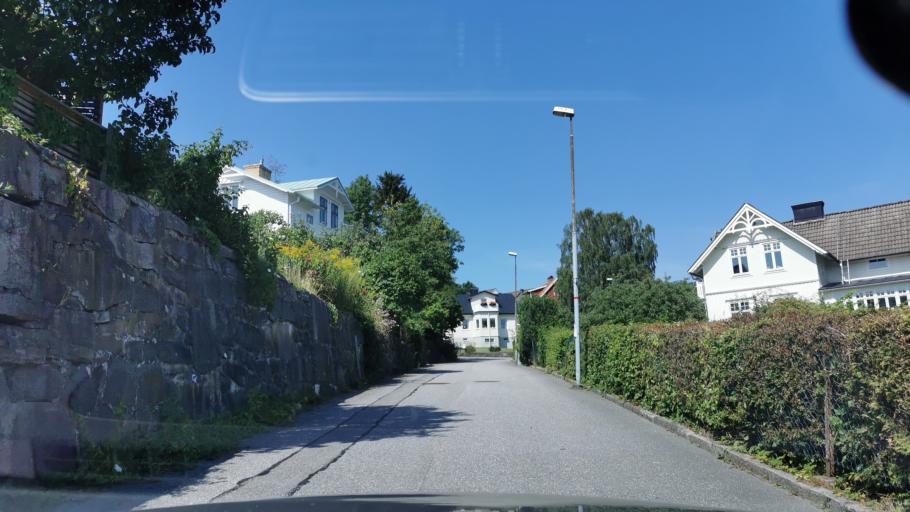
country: SE
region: Vaestra Goetaland
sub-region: Molndal
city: Moelndal
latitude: 57.6767
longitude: 12.0000
